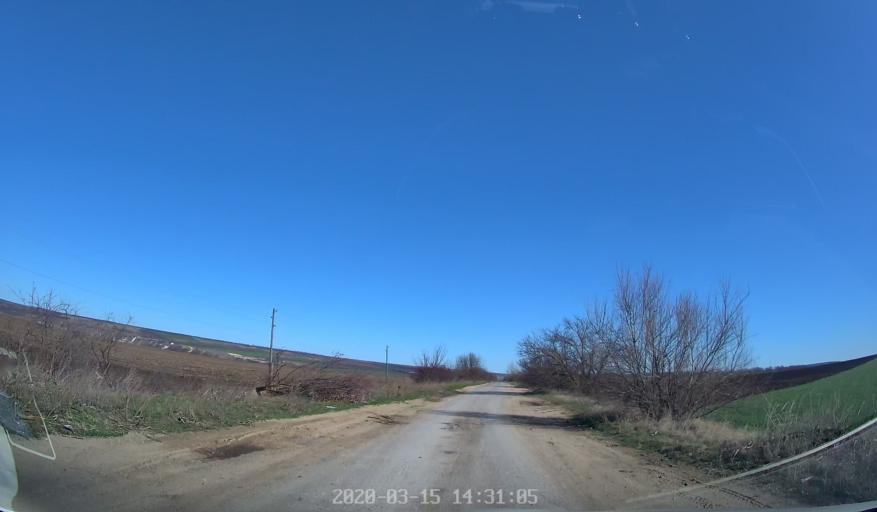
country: MD
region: Orhei
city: Orhei
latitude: 47.3455
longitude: 28.8917
